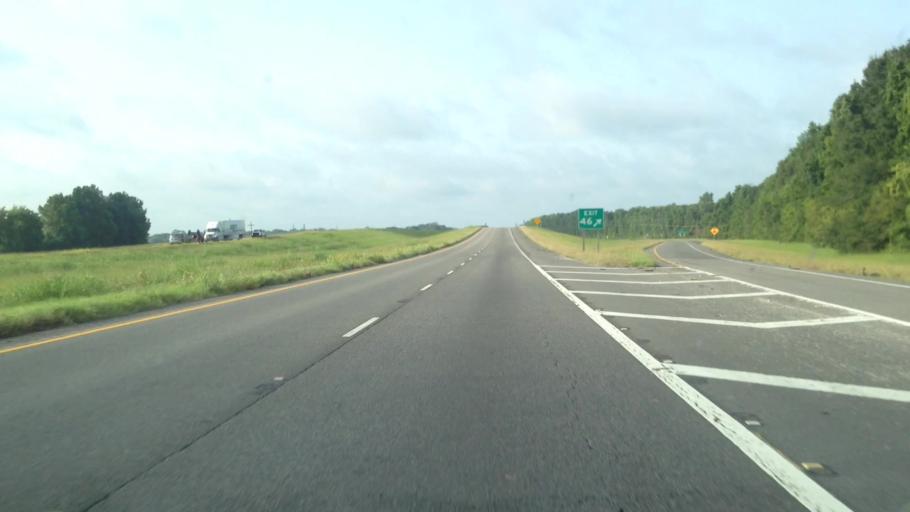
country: US
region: Louisiana
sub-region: Avoyelles Parish
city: Bunkie
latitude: 30.8701
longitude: -92.2281
